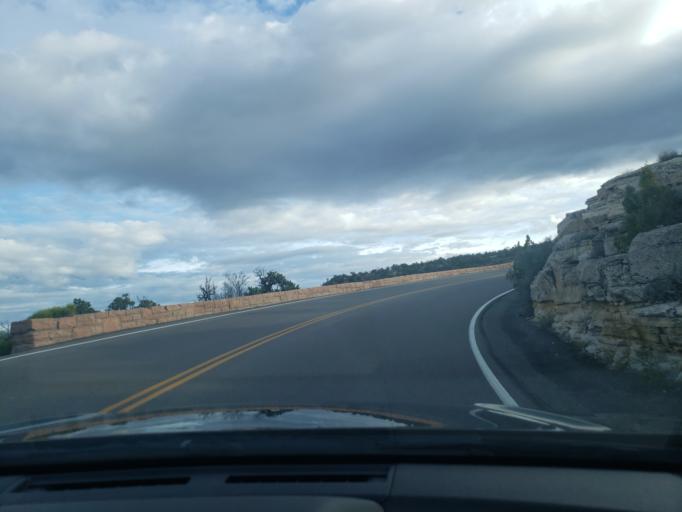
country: US
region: Colorado
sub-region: Mesa County
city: Redlands
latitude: 39.0329
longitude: -108.6471
